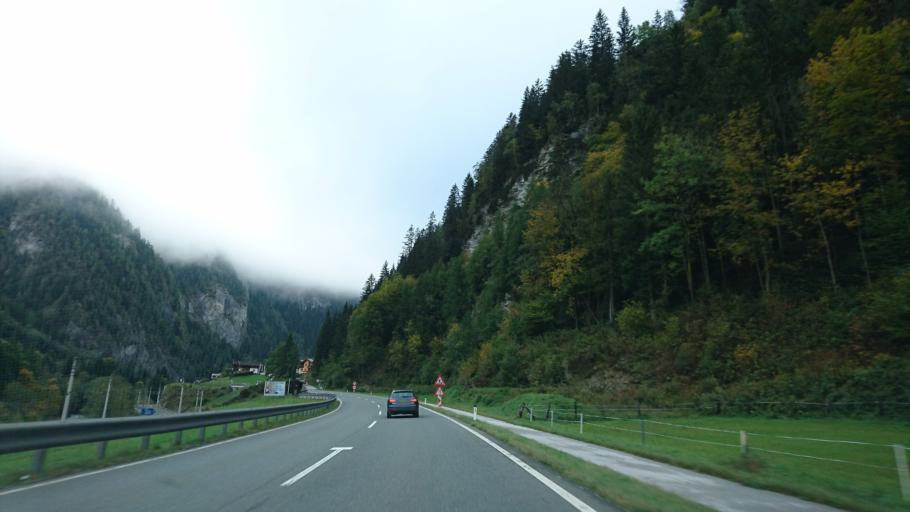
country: AT
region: Salzburg
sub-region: Politischer Bezirk Sankt Johann im Pongau
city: Dorfgastein
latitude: 47.2689
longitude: 13.0807
